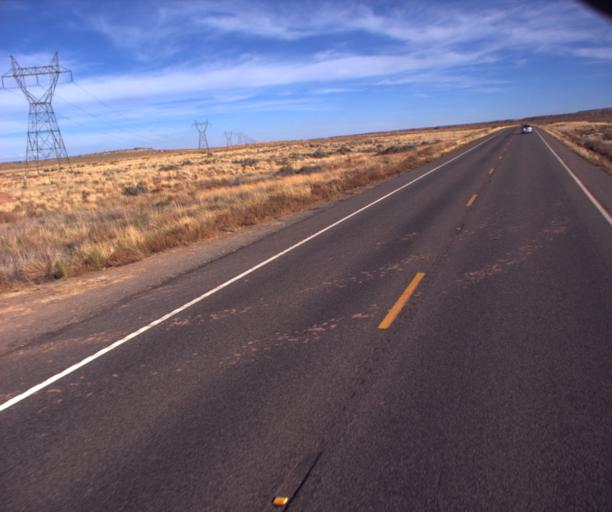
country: US
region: Arizona
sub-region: Apache County
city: Lukachukai
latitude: 36.9362
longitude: -109.2375
